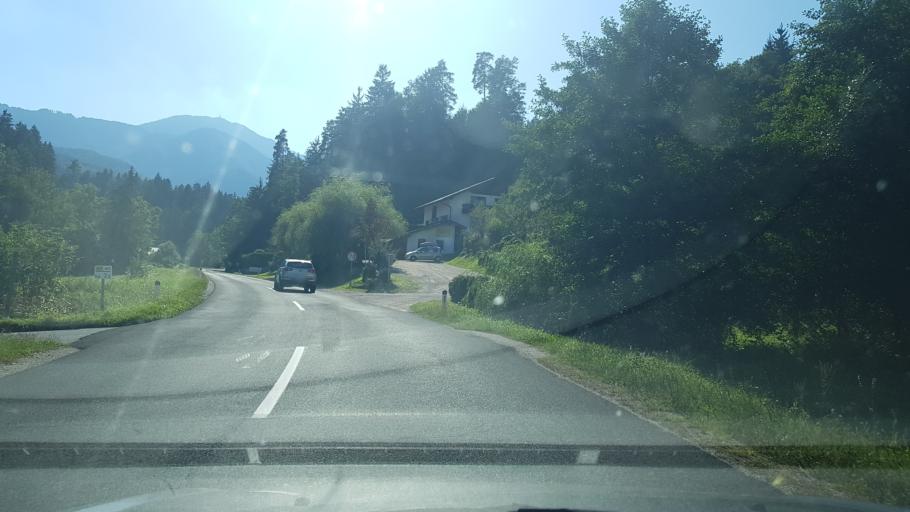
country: SI
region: Ravne na Koroskem
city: Kotlje
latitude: 46.5198
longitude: 15.0248
